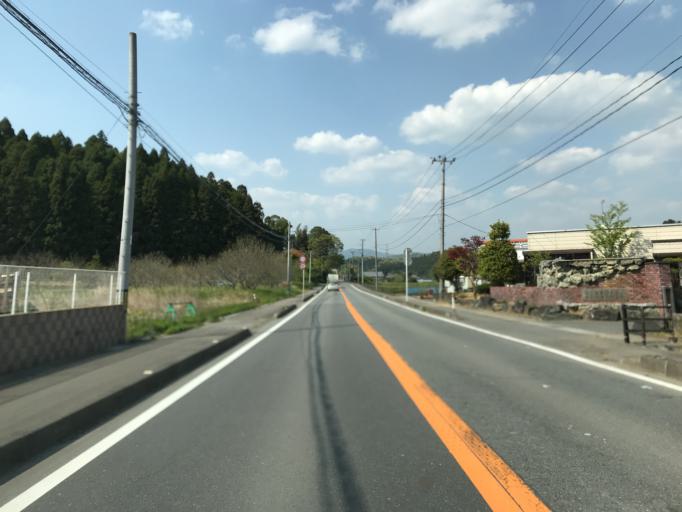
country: JP
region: Fukushima
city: Iwaki
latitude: 36.9430
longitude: 140.7683
